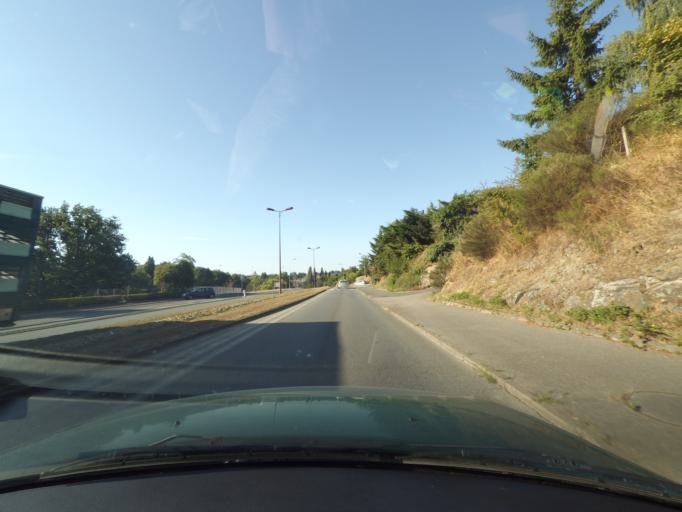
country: FR
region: Poitou-Charentes
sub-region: Departement des Deux-Sevres
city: Chatillon-sur-Thouet
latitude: 46.6599
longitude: -0.2395
